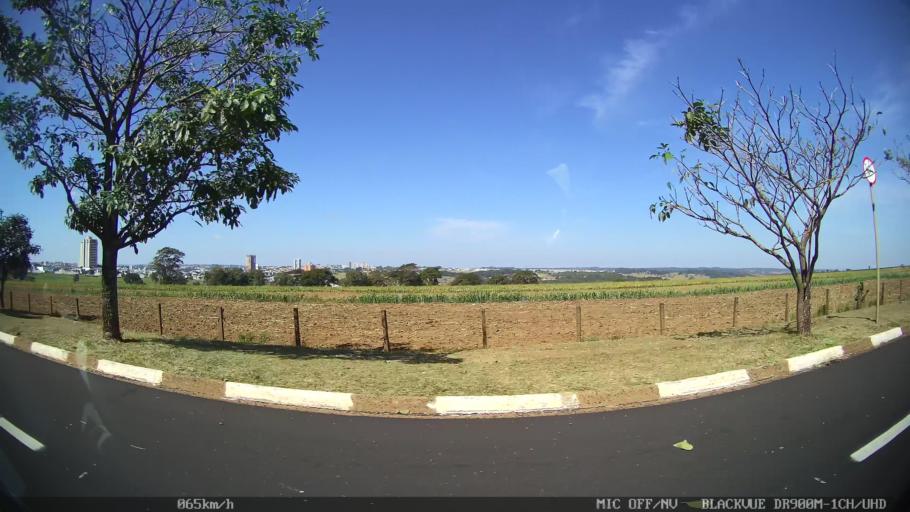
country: BR
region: Sao Paulo
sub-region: Franca
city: Franca
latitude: -20.5488
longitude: -47.4276
